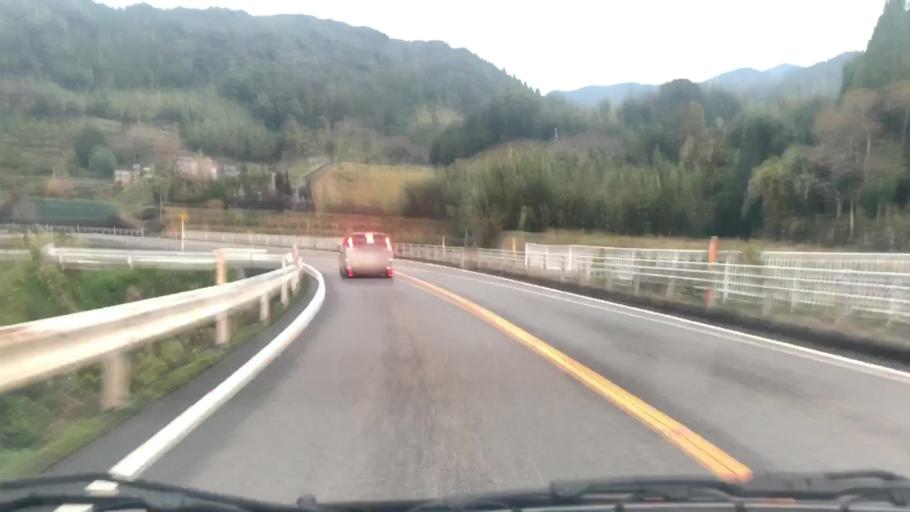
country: JP
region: Saga Prefecture
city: Ureshinomachi-shimojuku
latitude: 33.0548
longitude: 129.9374
